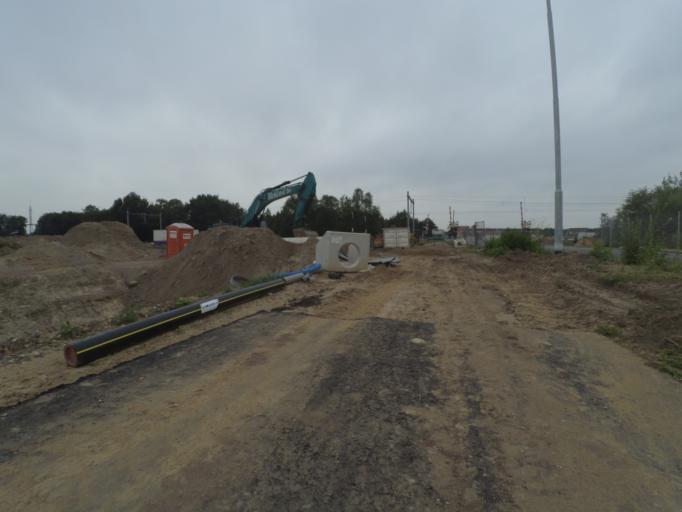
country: NL
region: Gelderland
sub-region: Gemeente Barneveld
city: Voorthuizen
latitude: 52.1654
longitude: 5.6166
